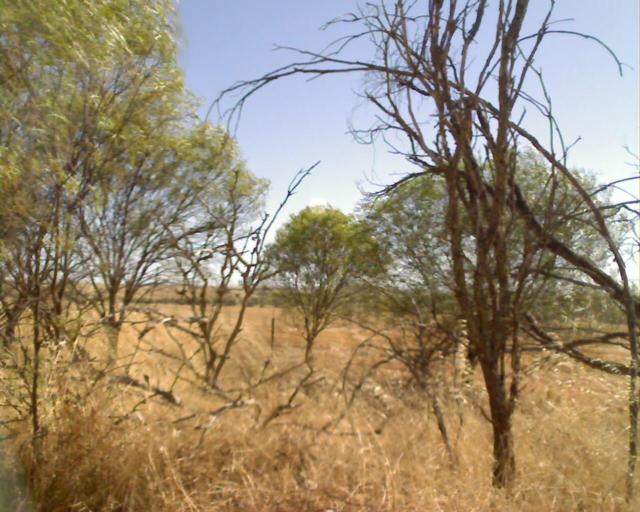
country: AU
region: Western Australia
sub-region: Irwin
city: Dongara
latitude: -29.1877
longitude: 115.4386
